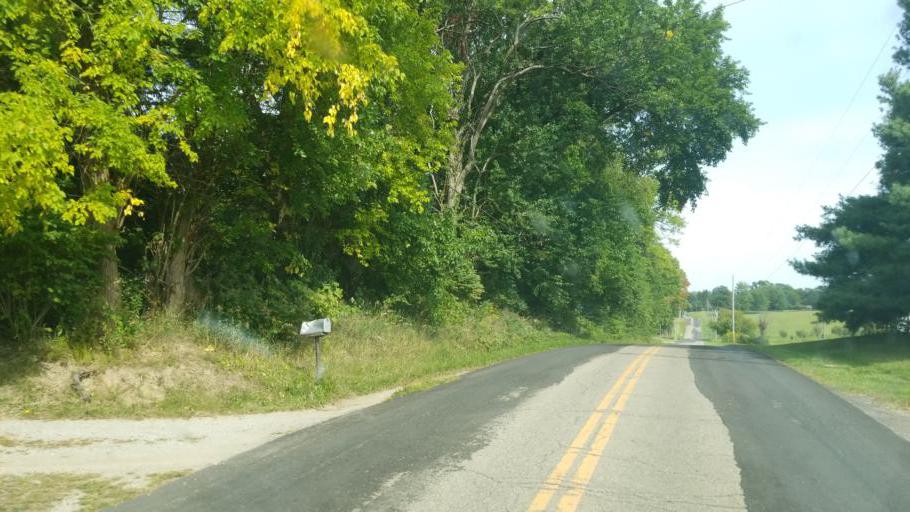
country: US
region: Ohio
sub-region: Knox County
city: Mount Vernon
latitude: 40.3825
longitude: -82.5511
